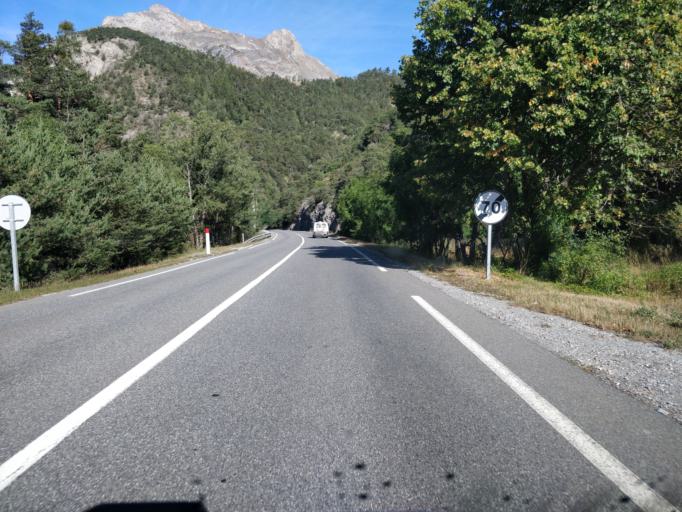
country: FR
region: Provence-Alpes-Cote d'Azur
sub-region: Departement des Alpes-de-Haute-Provence
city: Barcelonnette
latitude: 44.4001
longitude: 6.5299
